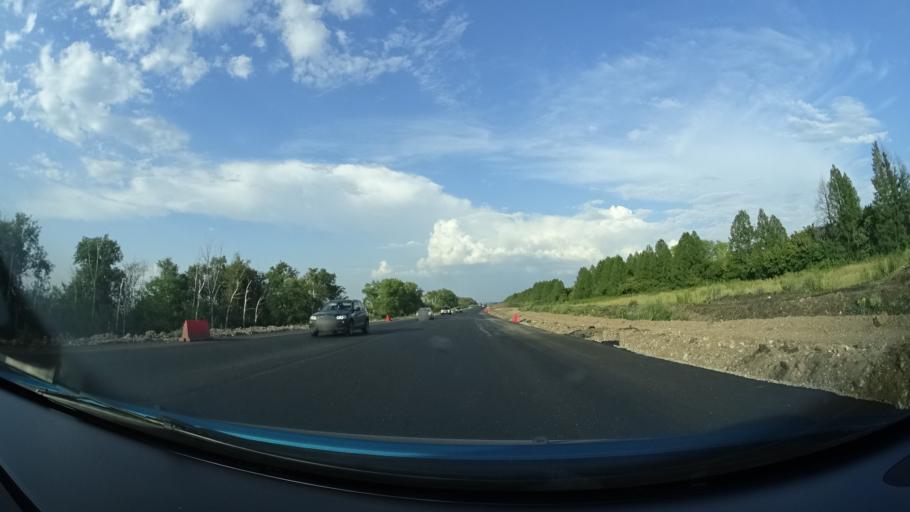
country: RU
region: Samara
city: Sukhodol
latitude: 53.7756
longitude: 50.9032
